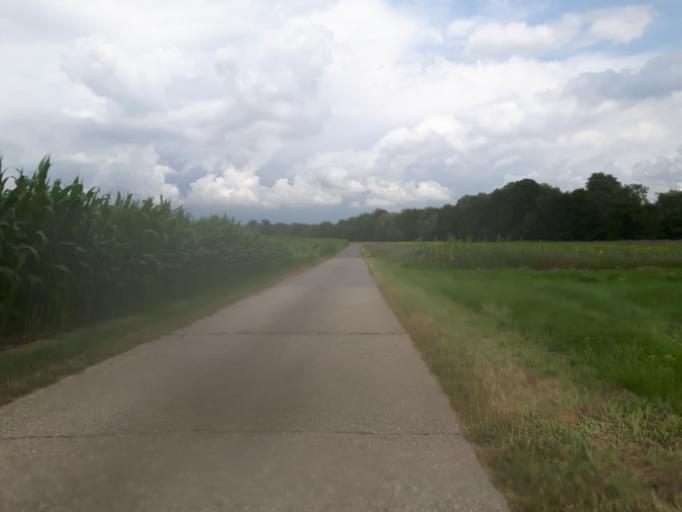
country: DE
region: Baden-Wuerttemberg
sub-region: Regierungsbezirk Stuttgart
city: Eppingen
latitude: 49.1480
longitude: 8.9319
